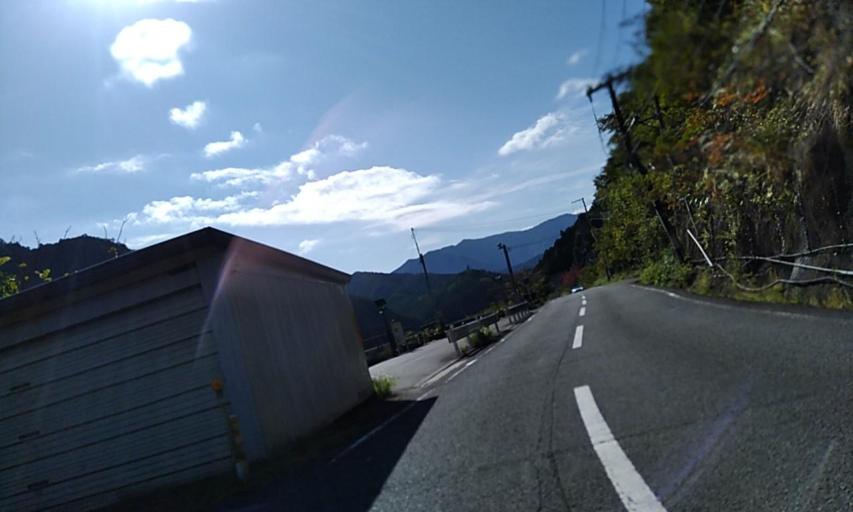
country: JP
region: Wakayama
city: Kainan
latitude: 34.0815
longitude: 135.3578
